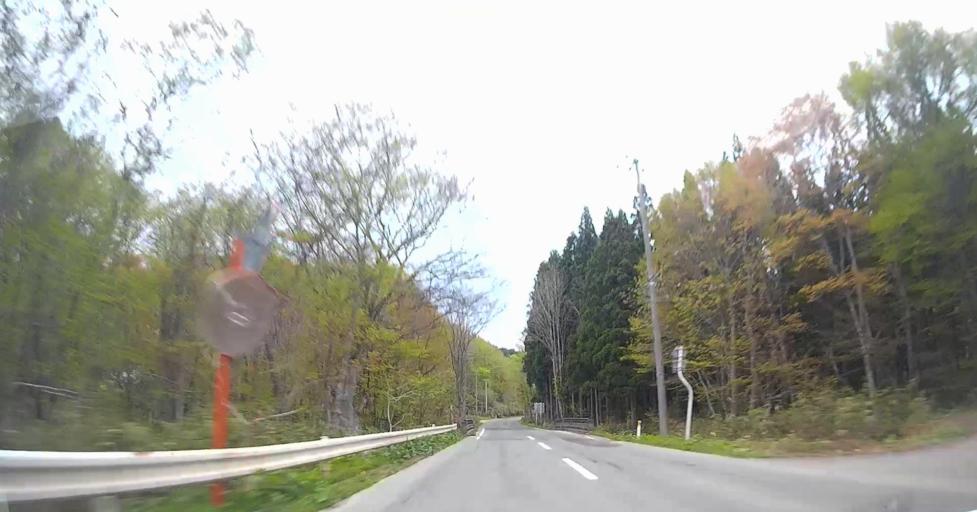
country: JP
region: Aomori
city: Goshogawara
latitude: 41.1172
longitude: 140.5251
